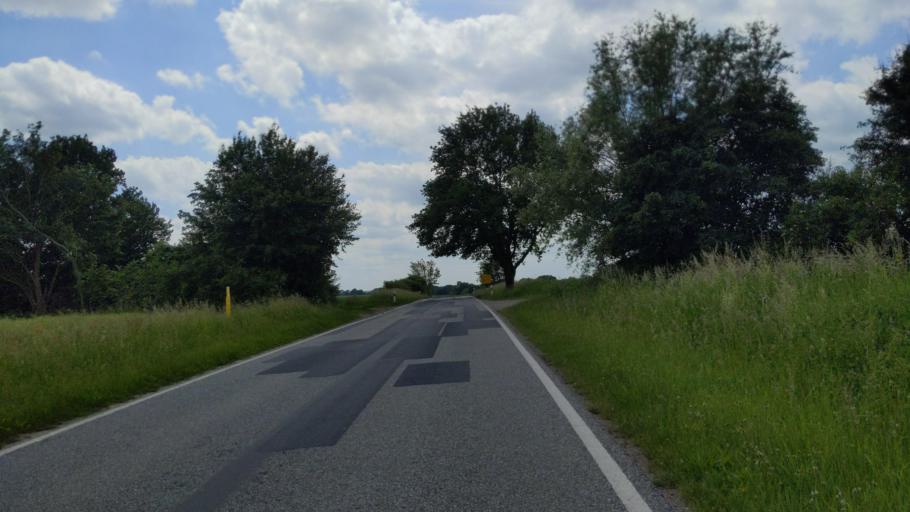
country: DE
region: Mecklenburg-Vorpommern
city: Selmsdorf
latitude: 53.8524
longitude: 10.8095
